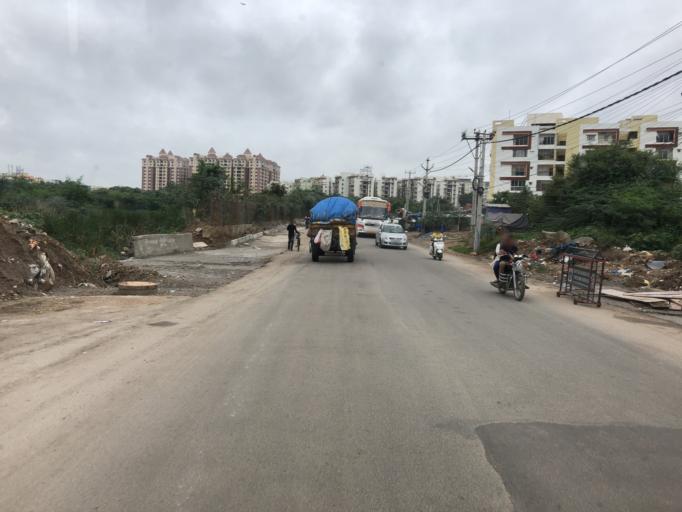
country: IN
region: Telangana
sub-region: Rangareddi
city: Kukatpalli
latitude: 17.4646
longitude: 78.3749
